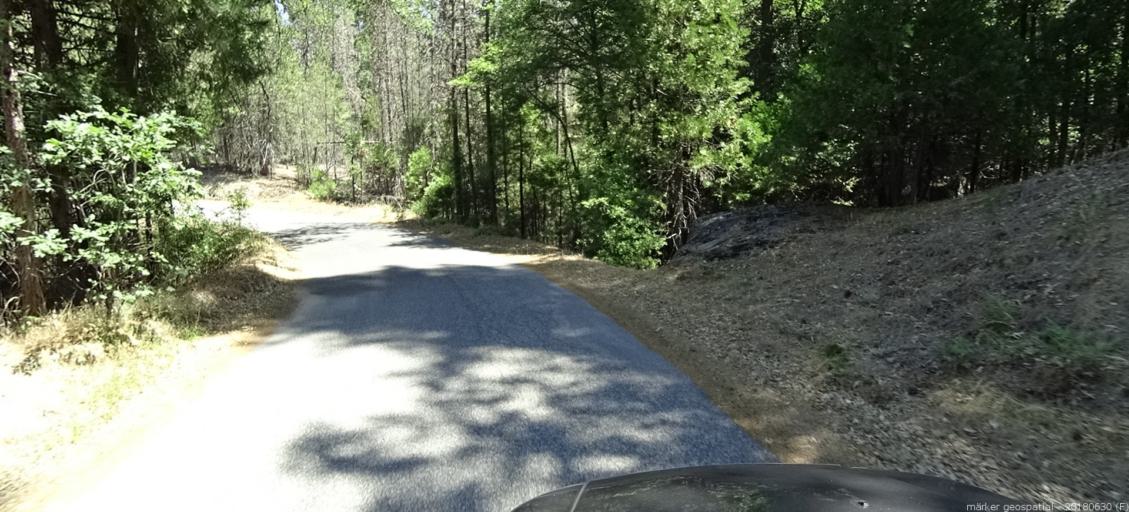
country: US
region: California
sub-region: Madera County
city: Oakhurst
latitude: 37.3645
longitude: -119.3518
